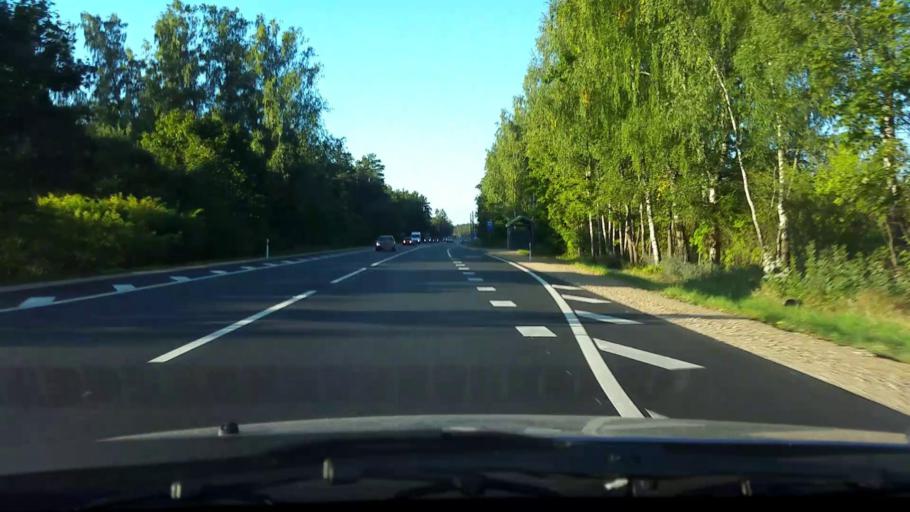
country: LV
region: Riga
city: Bergi
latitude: 57.0215
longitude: 24.3152
